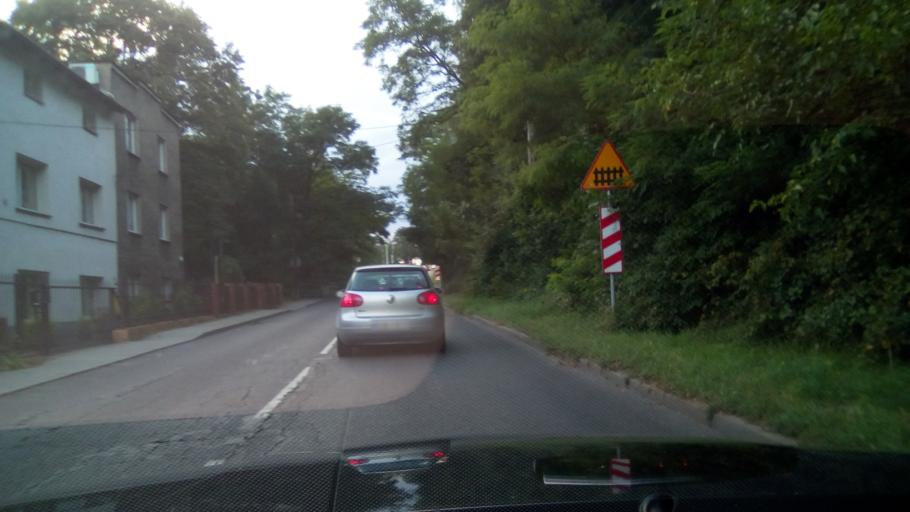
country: PL
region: Silesian Voivodeship
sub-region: Myslowice
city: Myslowice
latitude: 50.2072
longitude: 19.1521
